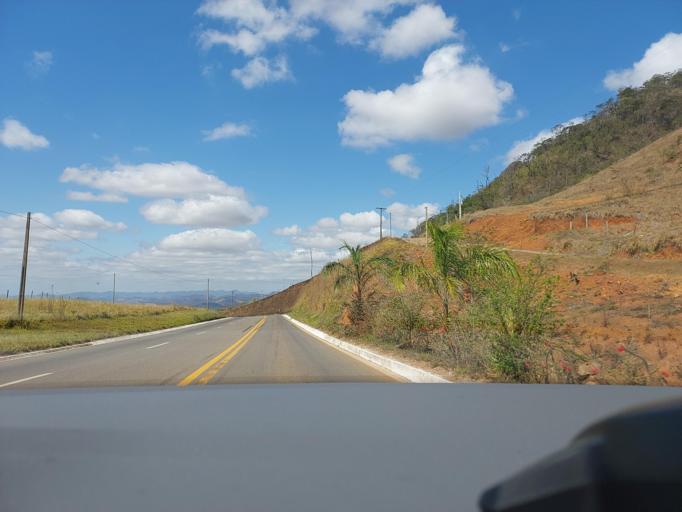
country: BR
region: Minas Gerais
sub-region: Muriae
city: Muriae
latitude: -21.0785
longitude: -42.4953
